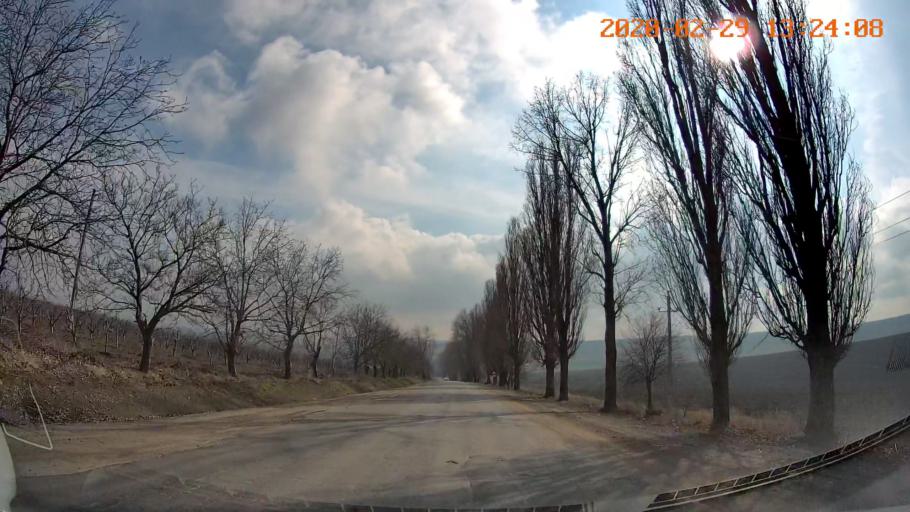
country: MD
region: Telenesti
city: Camenca
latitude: 47.9421
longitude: 28.6260
